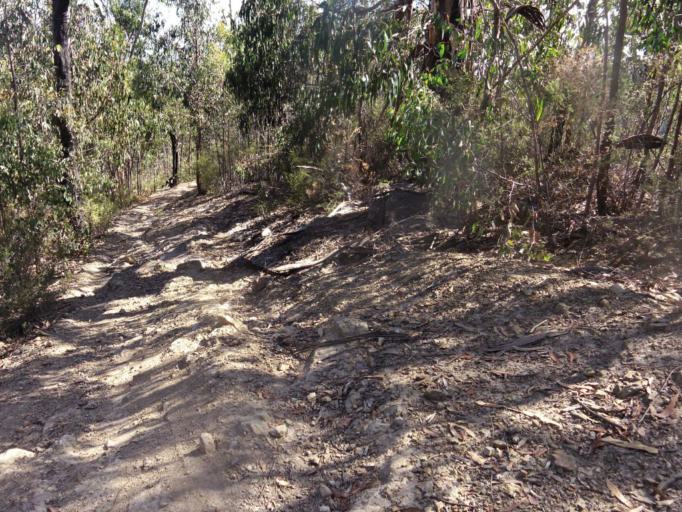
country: AU
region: Victoria
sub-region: Nillumbik
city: Saint Andrews
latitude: -37.5254
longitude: 145.3011
